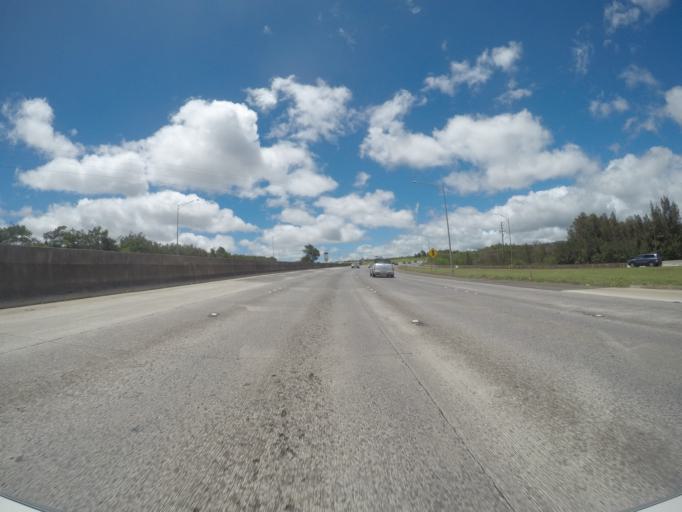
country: US
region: Hawaii
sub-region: Honolulu County
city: Waipio
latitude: 21.4304
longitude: -157.9967
